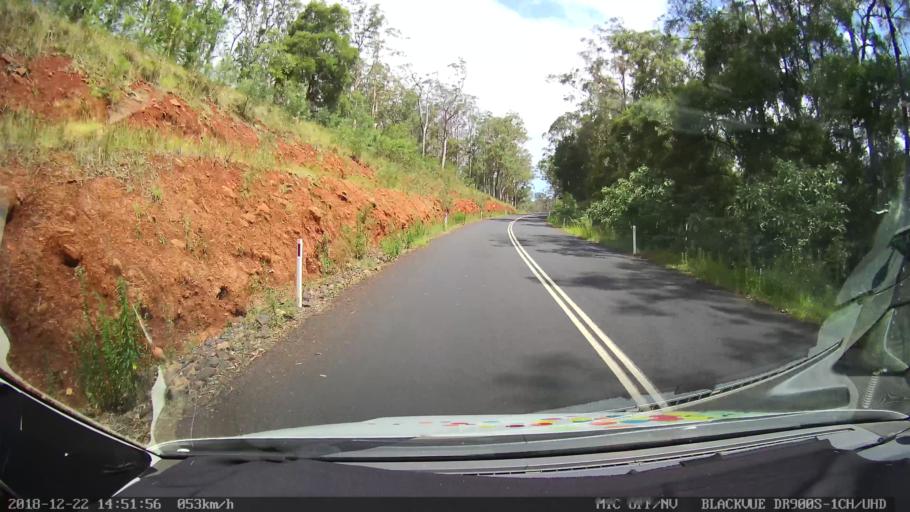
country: AU
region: New South Wales
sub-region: Bellingen
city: Dorrigo
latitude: -30.2059
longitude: 152.5436
